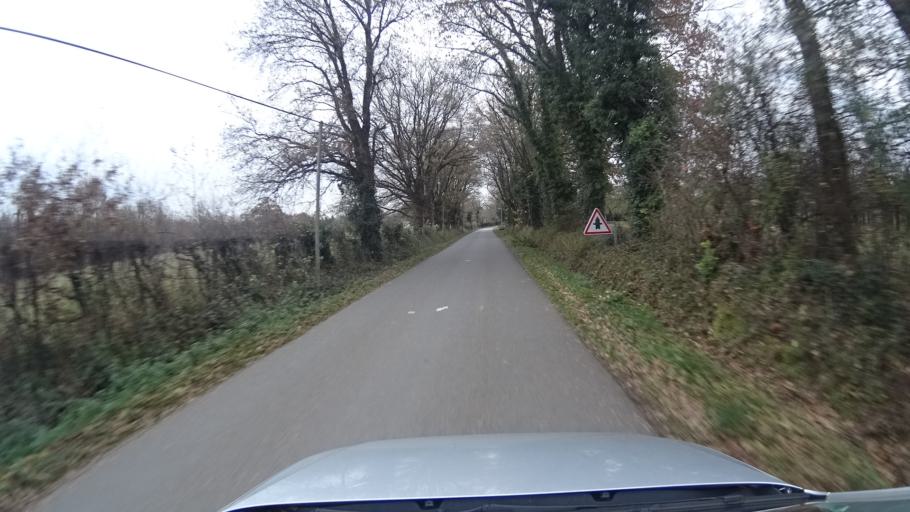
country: FR
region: Pays de la Loire
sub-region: Departement de la Loire-Atlantique
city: Avessac
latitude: 47.6747
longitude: -1.9205
